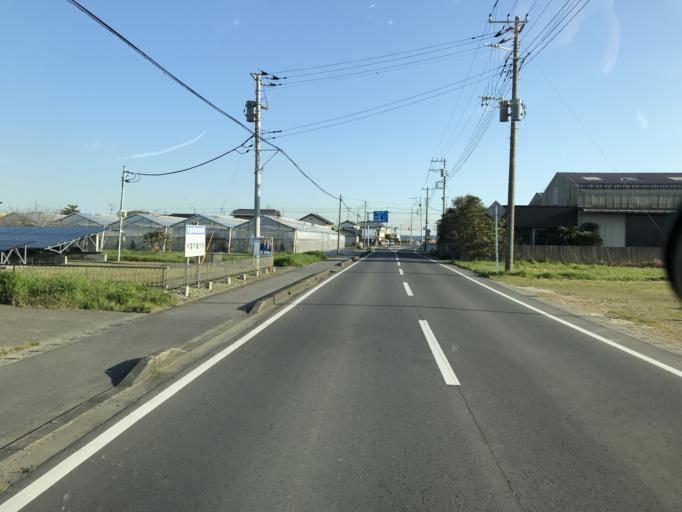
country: JP
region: Chiba
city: Asahi
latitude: 35.7107
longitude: 140.6889
